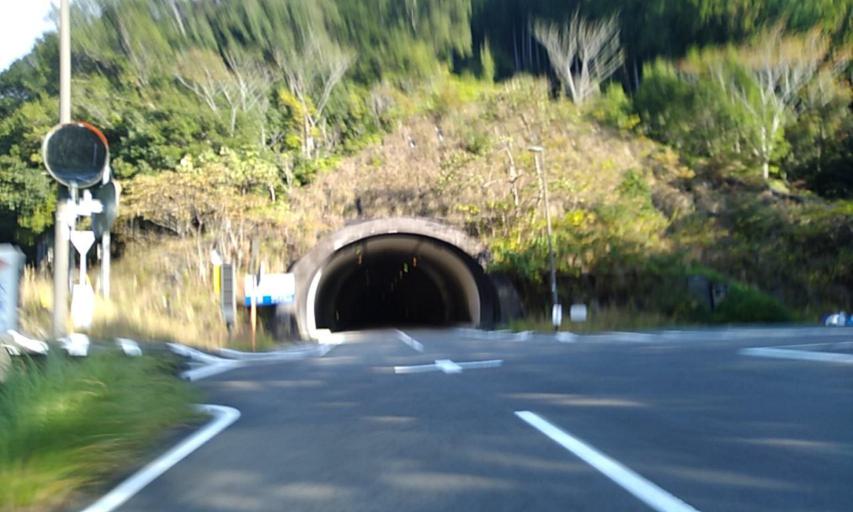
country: JP
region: Wakayama
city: Shingu
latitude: 33.8951
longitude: 135.8796
